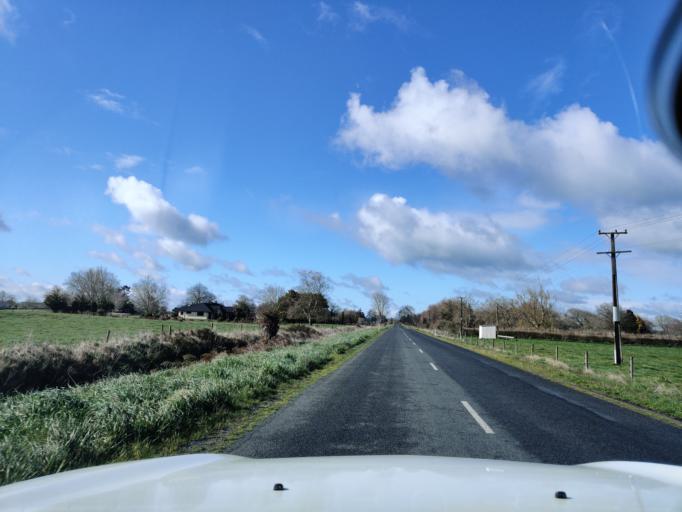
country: NZ
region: Waikato
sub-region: Waikato District
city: Ngaruawahia
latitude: -37.6080
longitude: 175.3073
